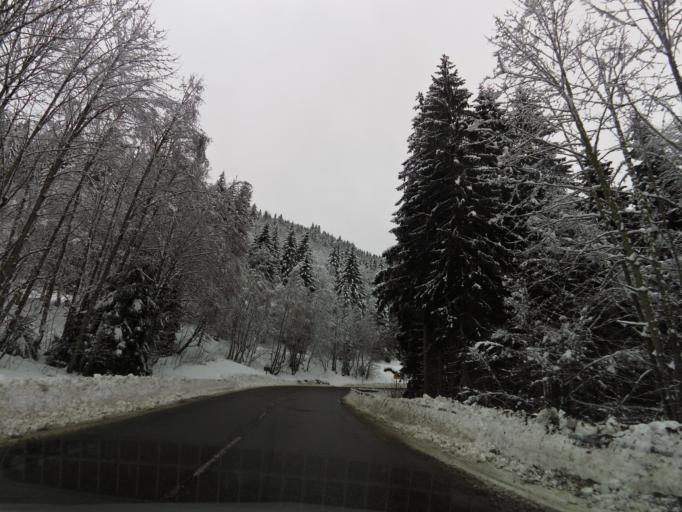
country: FR
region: Rhone-Alpes
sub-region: Departement de la Haute-Savoie
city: Morzine
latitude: 46.1759
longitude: 6.6813
